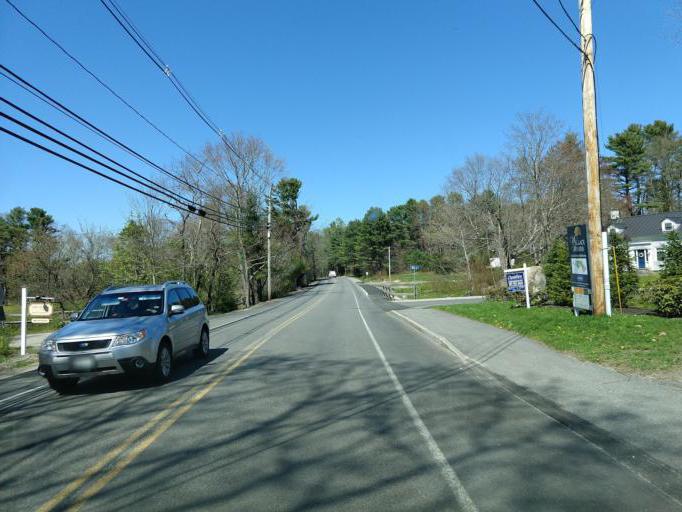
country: US
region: Maine
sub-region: York County
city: Kennebunkport
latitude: 43.3676
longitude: -70.4743
